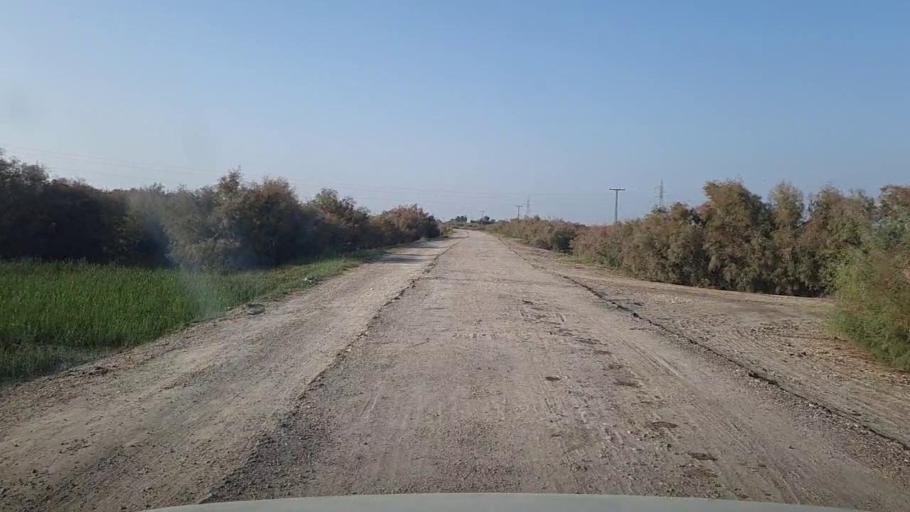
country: PK
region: Sindh
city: Kandhkot
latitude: 28.3048
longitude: 69.3287
